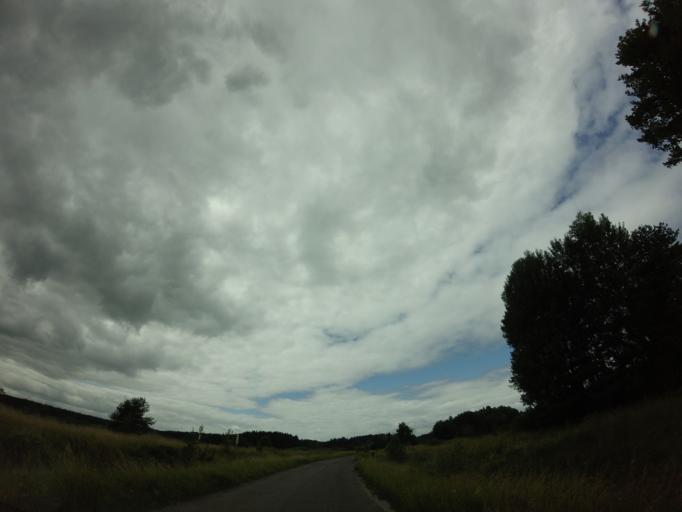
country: PL
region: West Pomeranian Voivodeship
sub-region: Powiat stargardzki
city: Insko
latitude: 53.3656
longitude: 15.6020
